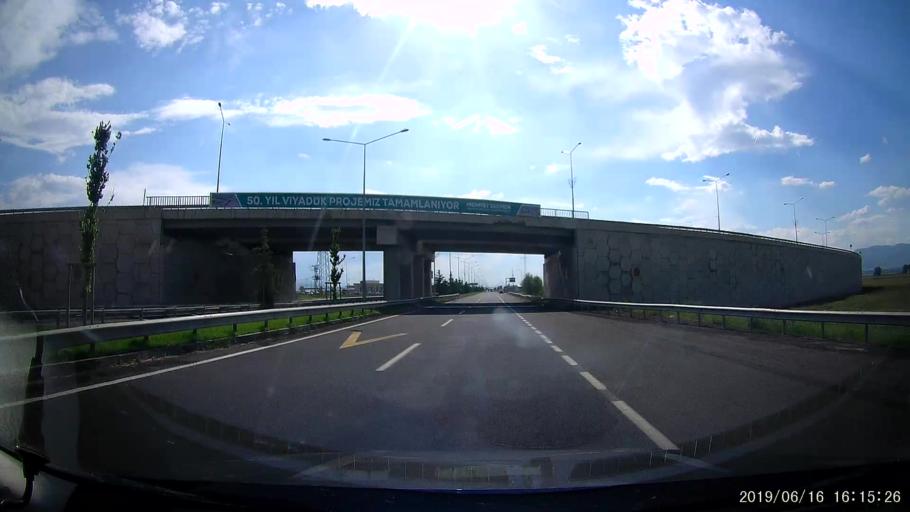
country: TR
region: Erzurum
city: Erzurum
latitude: 39.9619
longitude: 41.2265
